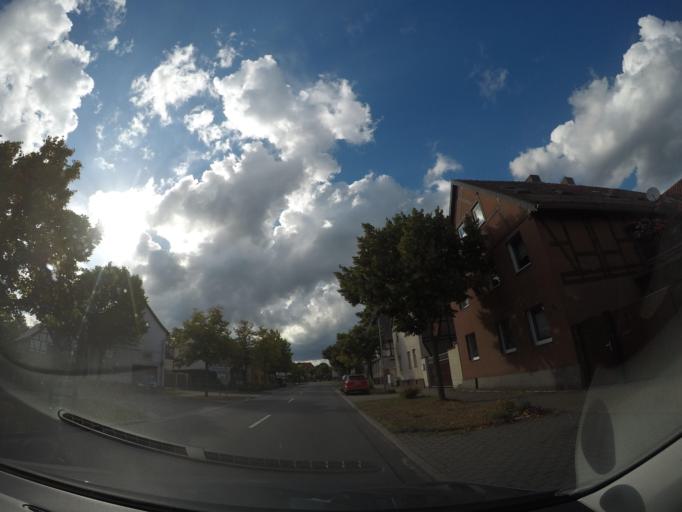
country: DE
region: Saxony-Anhalt
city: Bulstringen
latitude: 52.3213
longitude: 11.3449
